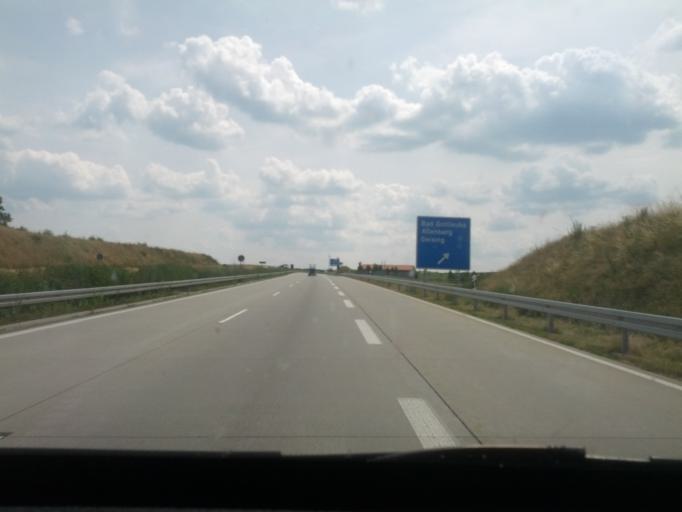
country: DE
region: Saxony
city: Liebstadt
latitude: 50.8348
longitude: 13.8839
